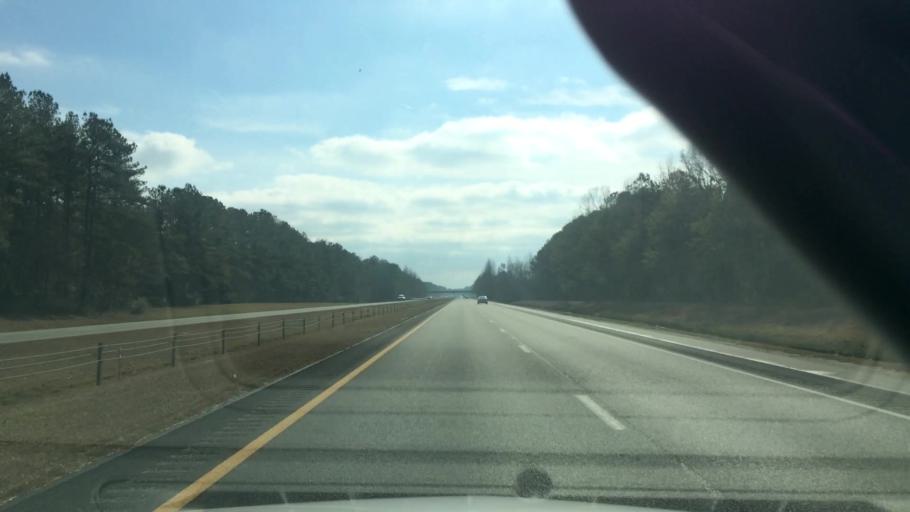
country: US
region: North Carolina
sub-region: Pender County
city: Rocky Point
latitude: 34.4891
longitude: -77.8779
